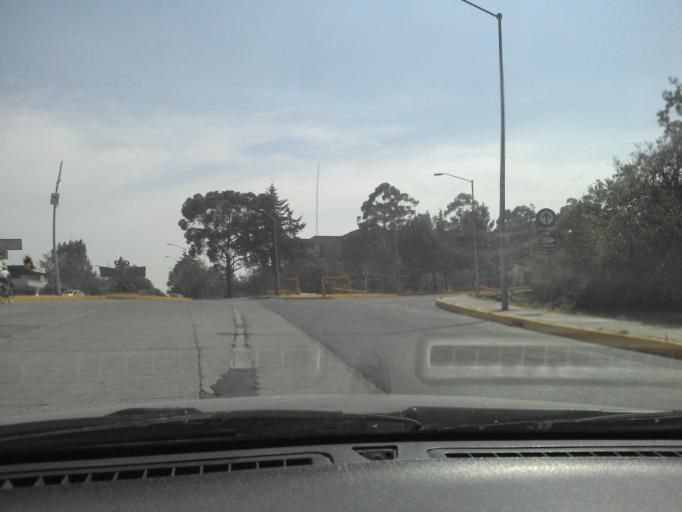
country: MX
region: Mexico City
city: Magdalena Contreras
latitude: 19.3176
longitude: -99.1872
